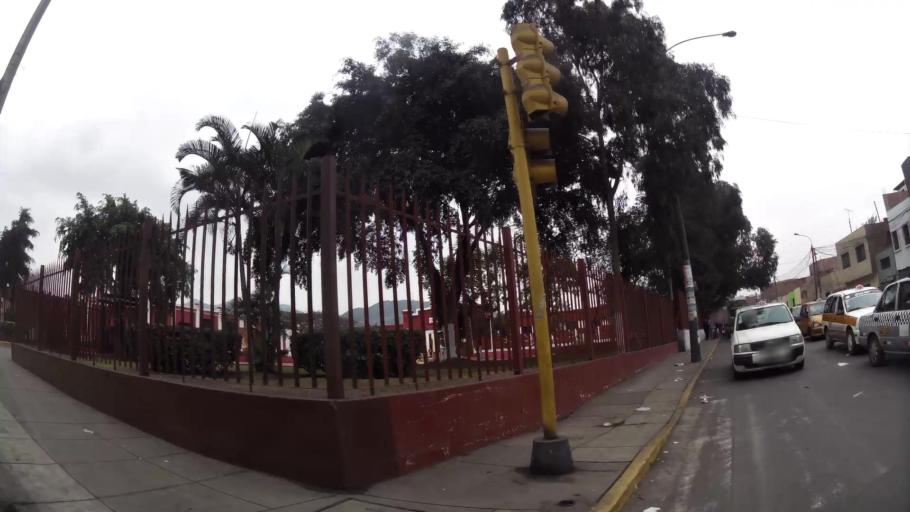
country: PE
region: Lima
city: Lima
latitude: -12.0536
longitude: -77.0122
